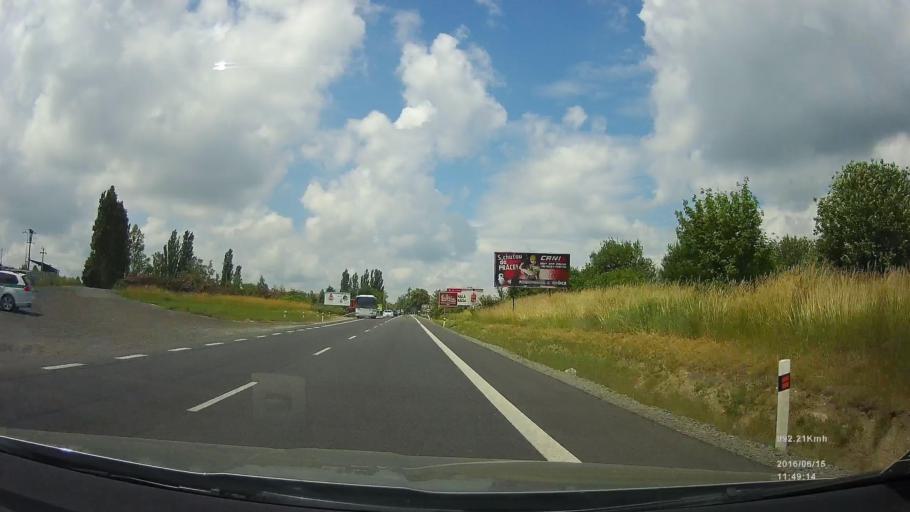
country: SK
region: Kosicky
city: Kosice
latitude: 48.7350
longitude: 21.3042
